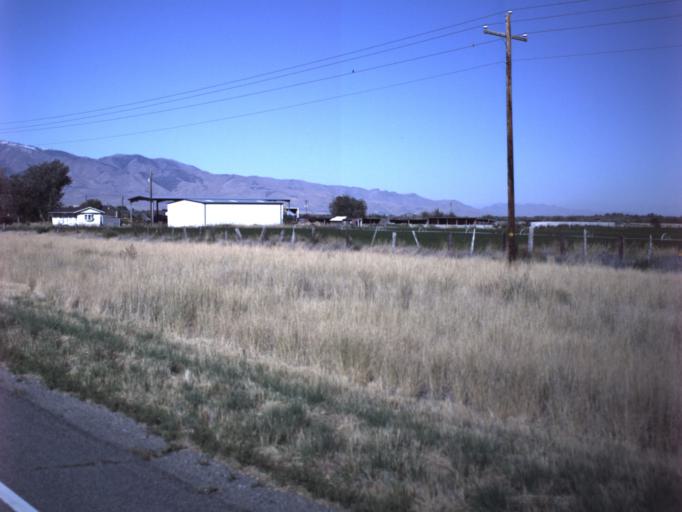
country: US
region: Utah
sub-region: Tooele County
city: Grantsville
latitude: 40.5997
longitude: -112.4124
